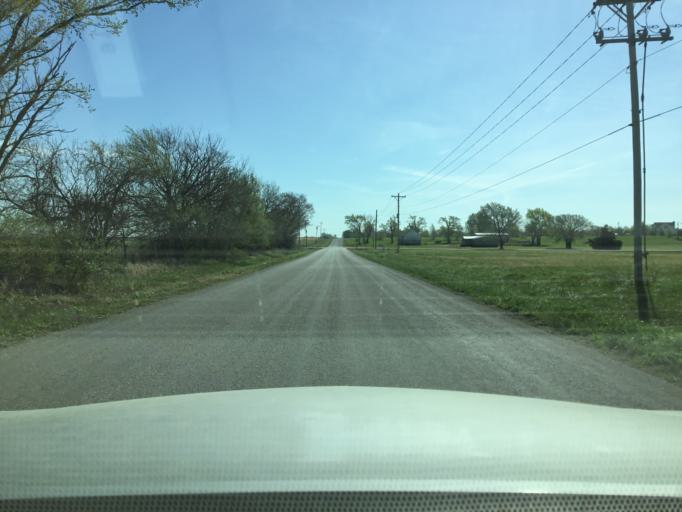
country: US
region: Kansas
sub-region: Neosho County
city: Chanute
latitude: 37.6458
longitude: -95.4458
